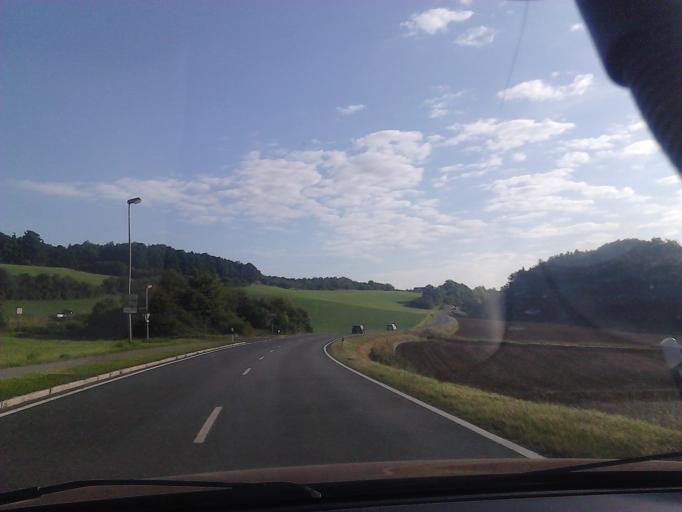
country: DE
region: Bavaria
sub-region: Upper Franconia
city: Weitramsdorf
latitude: 50.2603
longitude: 10.8899
